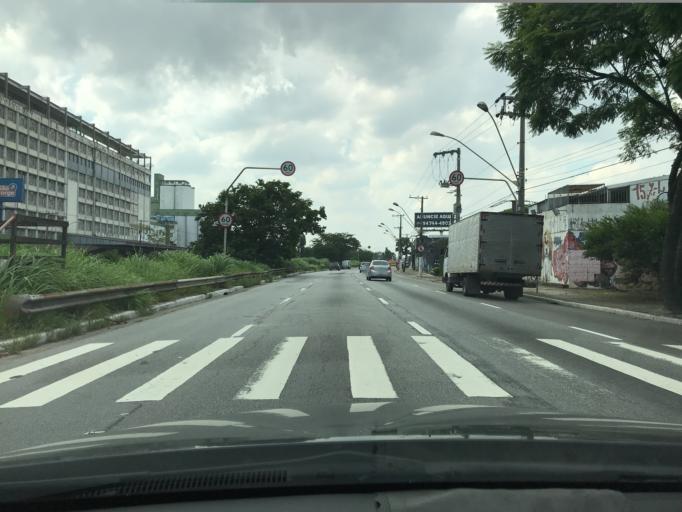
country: BR
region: Sao Paulo
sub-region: Santo Andre
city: Santo Andre
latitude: -23.6425
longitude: -46.5327
